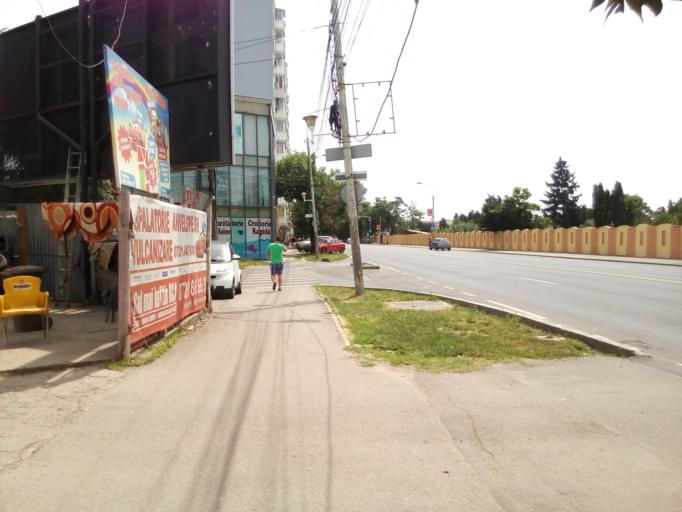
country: RO
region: Timis
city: Timisoara
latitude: 45.7376
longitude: 21.2096
